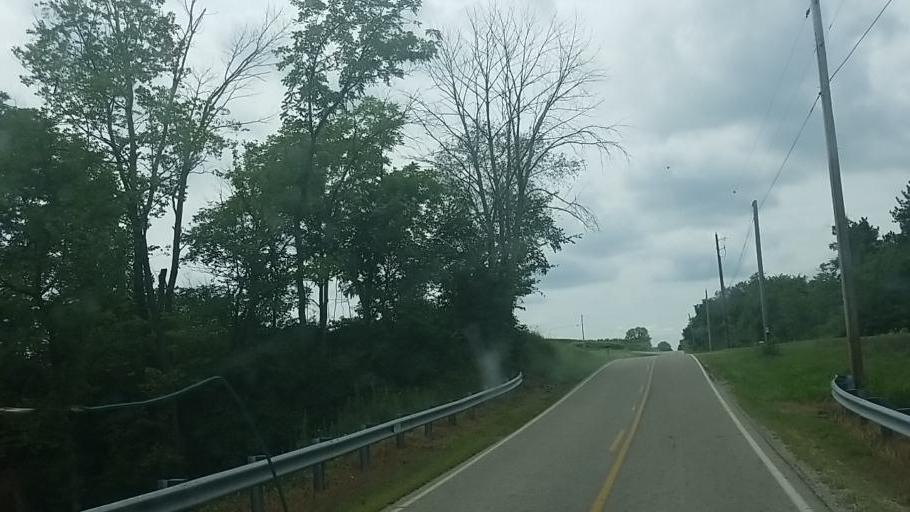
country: US
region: Ohio
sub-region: Fairfield County
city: Lithopolis
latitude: 39.7520
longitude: -82.8449
